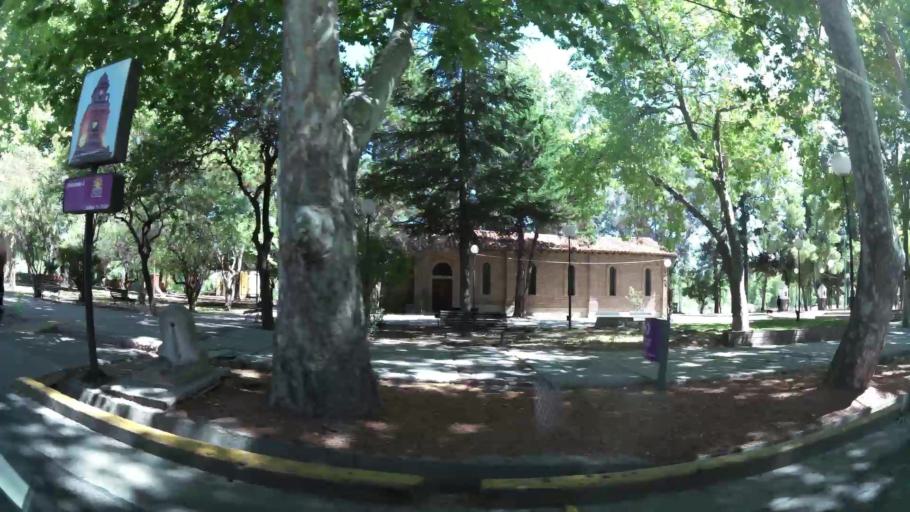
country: AR
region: Mendoza
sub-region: Departamento de Godoy Cruz
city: Godoy Cruz
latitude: -32.9586
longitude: -68.8522
